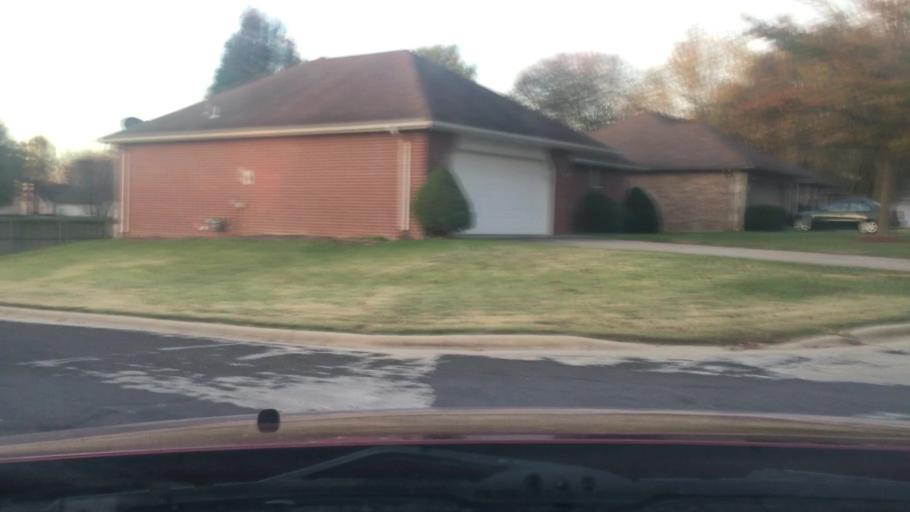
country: US
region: Missouri
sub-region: Greene County
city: Springfield
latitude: 37.2277
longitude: -93.2077
